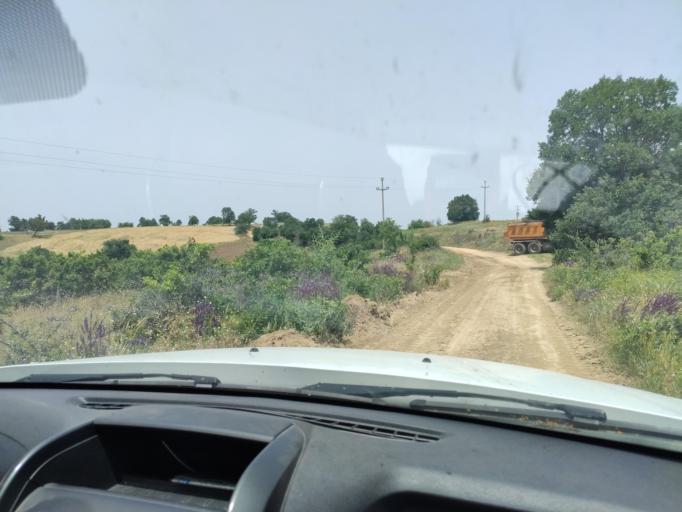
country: MK
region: Radovis
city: Radovish
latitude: 41.6750
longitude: 22.4034
